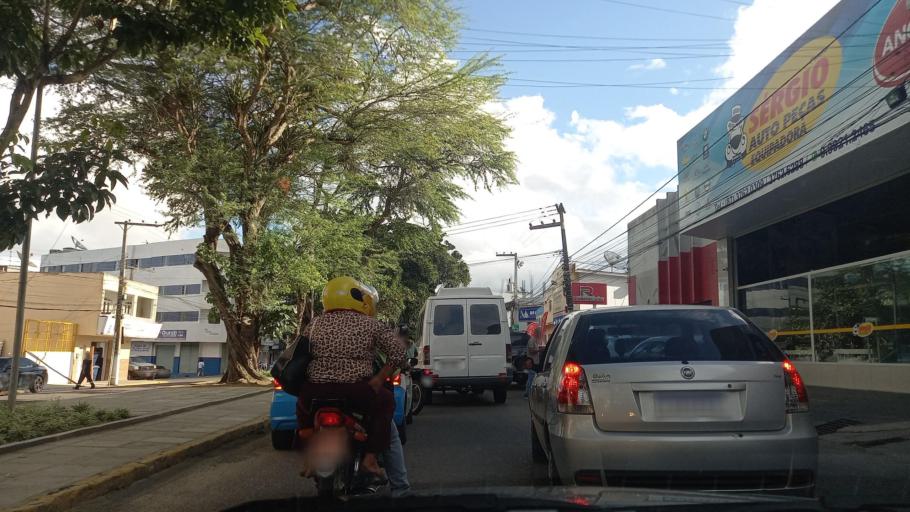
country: BR
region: Pernambuco
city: Garanhuns
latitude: -8.8847
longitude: -36.4890
